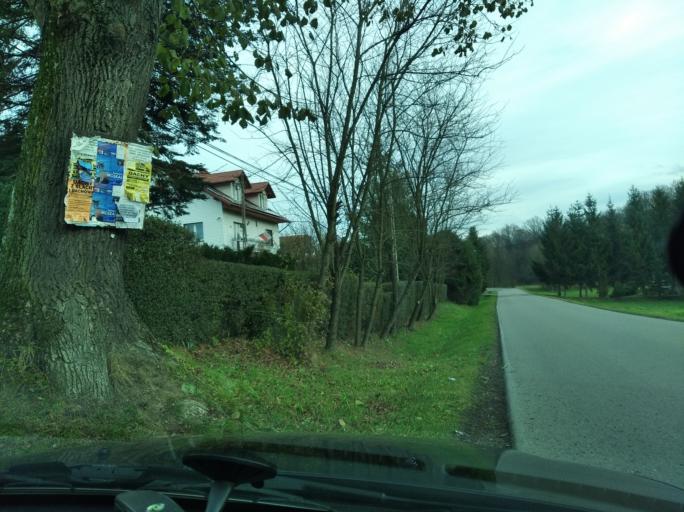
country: PL
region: Subcarpathian Voivodeship
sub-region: Powiat ropczycko-sedziszowski
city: Iwierzyce
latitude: 49.9466
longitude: 21.7365
